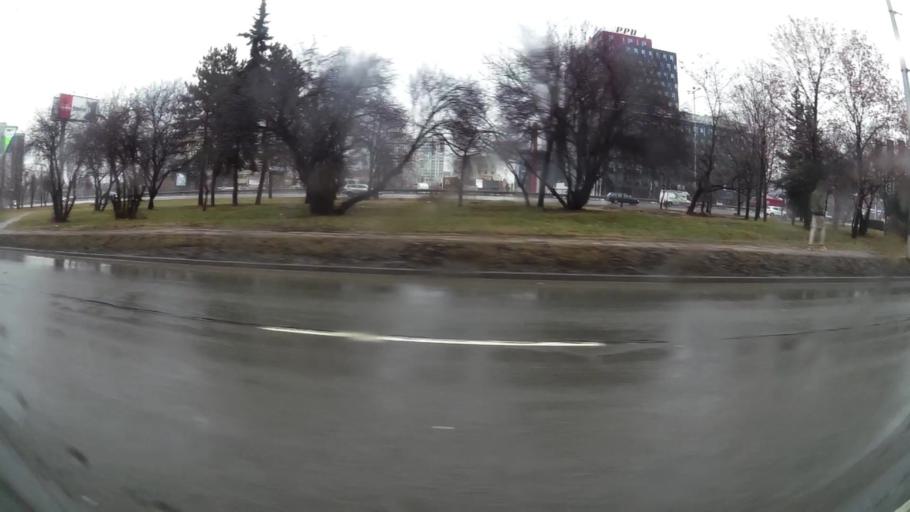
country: BG
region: Sofia-Capital
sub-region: Stolichna Obshtina
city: Sofia
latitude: 42.6608
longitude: 23.3783
